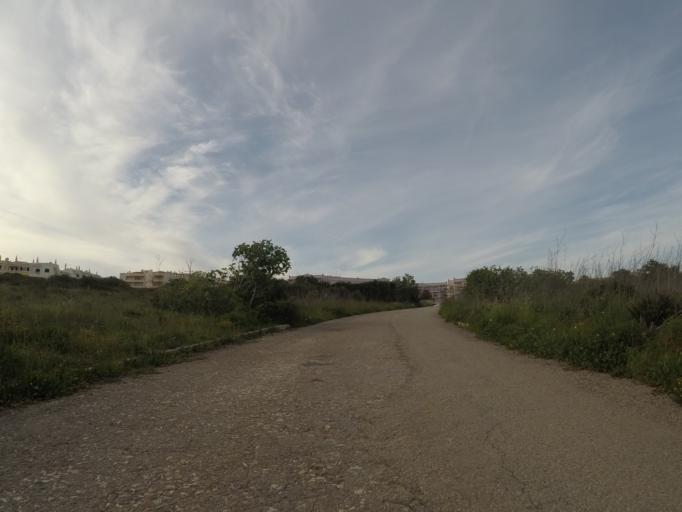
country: PT
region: Faro
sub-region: Lagos
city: Lagos
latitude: 37.0854
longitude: -8.7356
